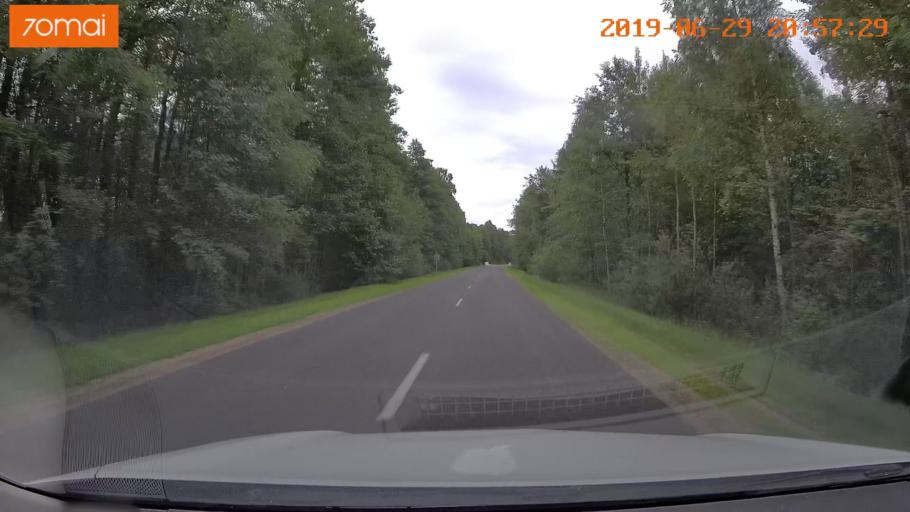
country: BY
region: Brest
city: Hantsavichy
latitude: 52.7197
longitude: 26.3712
